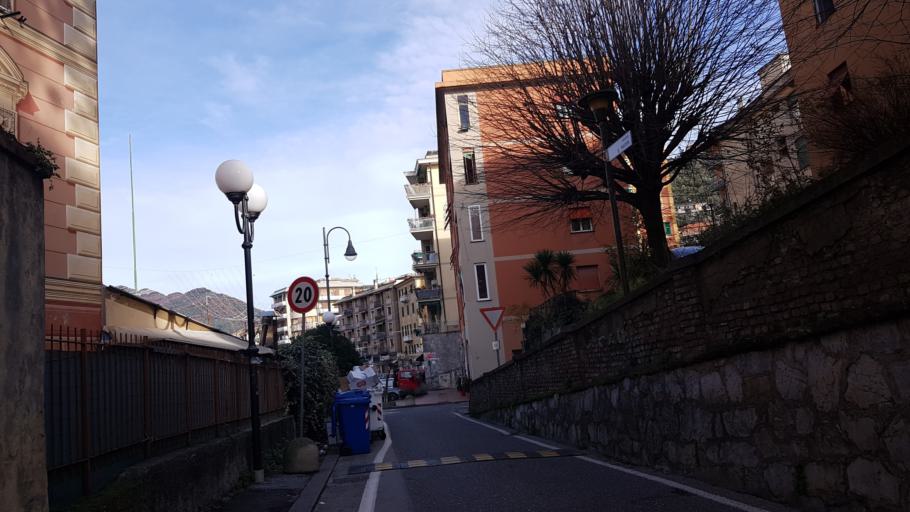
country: IT
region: Liguria
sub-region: Provincia di Genova
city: Recco
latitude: 44.3637
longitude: 9.1461
